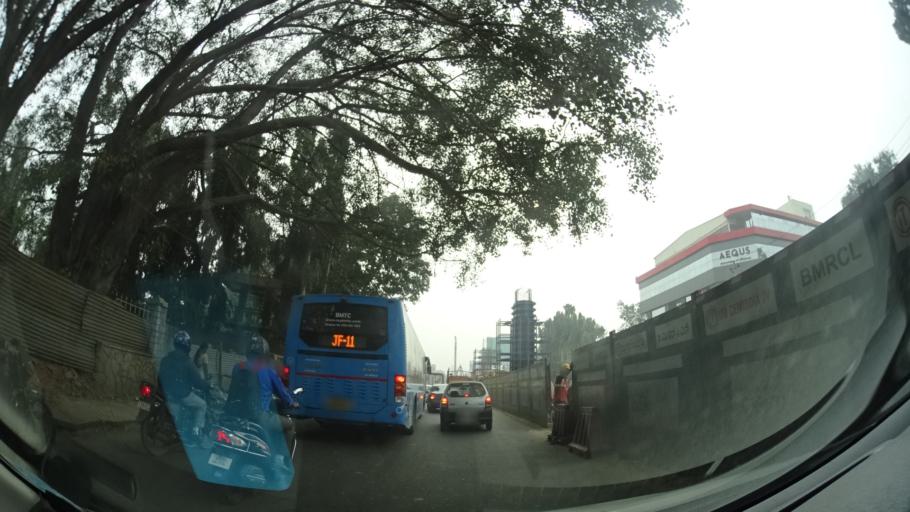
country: IN
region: Karnataka
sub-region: Bangalore Urban
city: Bangalore
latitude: 12.9971
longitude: 77.6912
